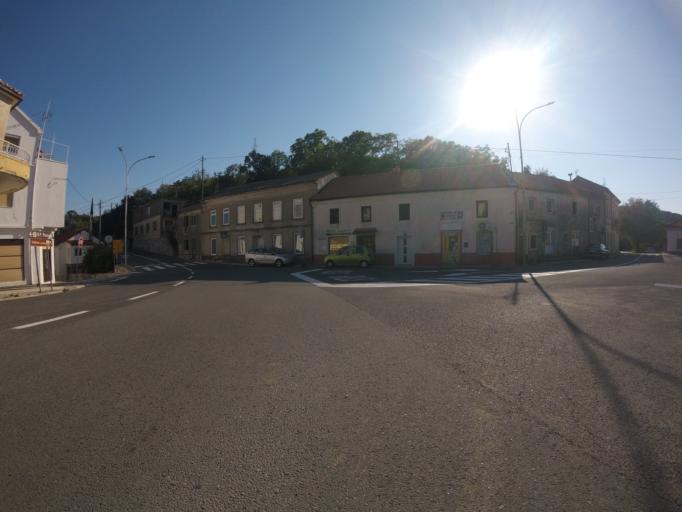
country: HR
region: Primorsko-Goranska
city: Hreljin
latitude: 45.2608
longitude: 14.6112
